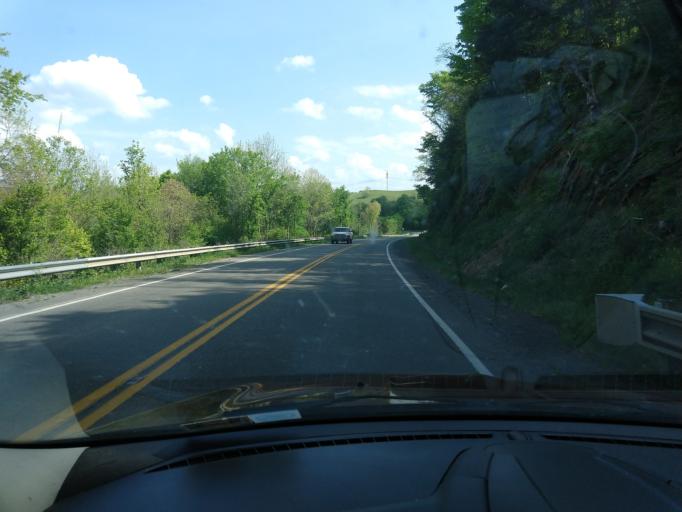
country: US
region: Virginia
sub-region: Russell County
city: Honaker
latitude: 36.9788
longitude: -81.9406
